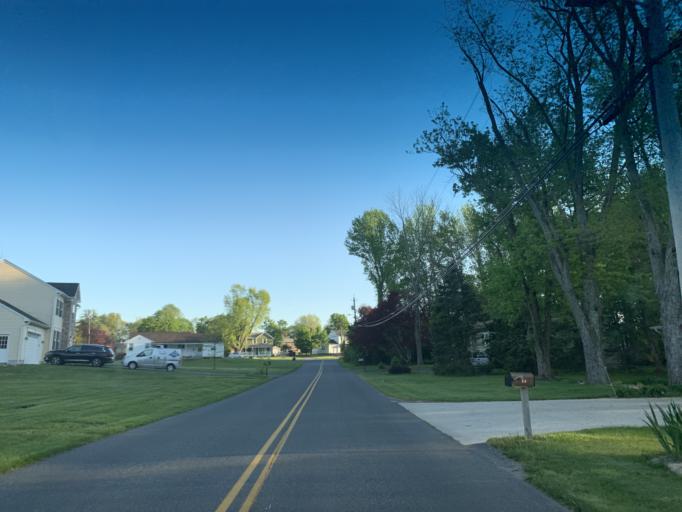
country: US
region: Maryland
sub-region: Harford County
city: Aberdeen
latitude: 39.5290
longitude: -76.1747
